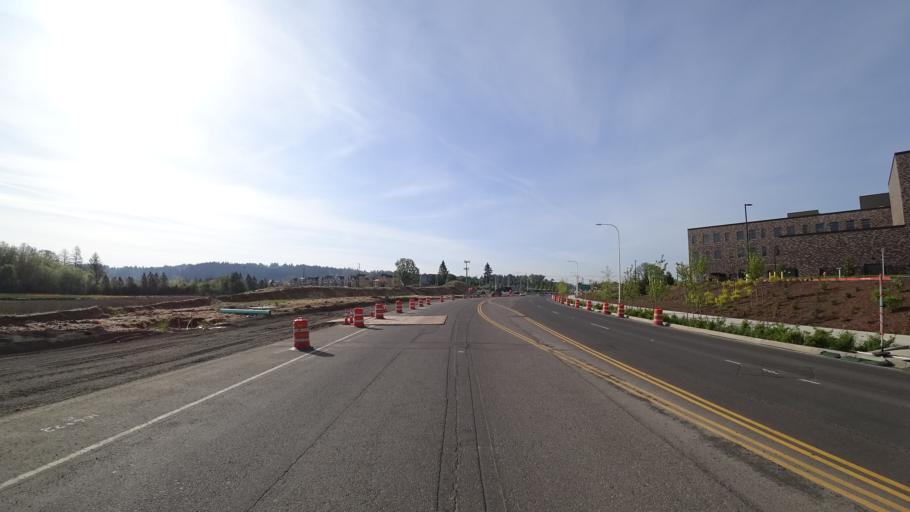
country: US
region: Oregon
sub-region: Washington County
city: King City
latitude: 45.4282
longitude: -122.8545
